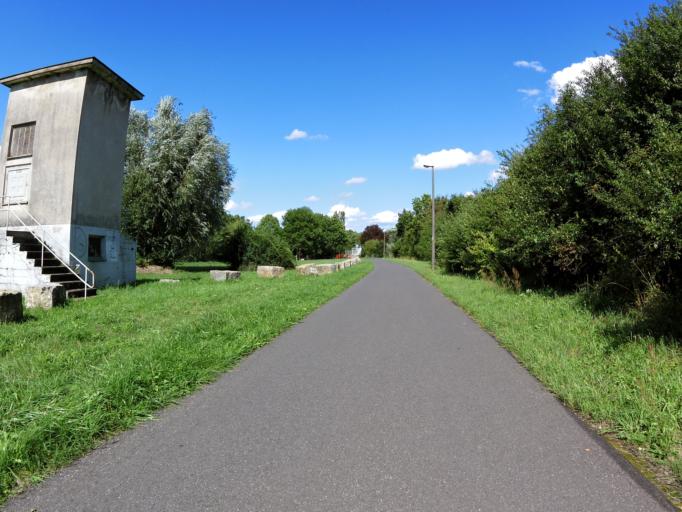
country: DE
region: Bavaria
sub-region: Regierungsbezirk Unterfranken
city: Kitzingen
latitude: 49.7279
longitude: 10.1673
